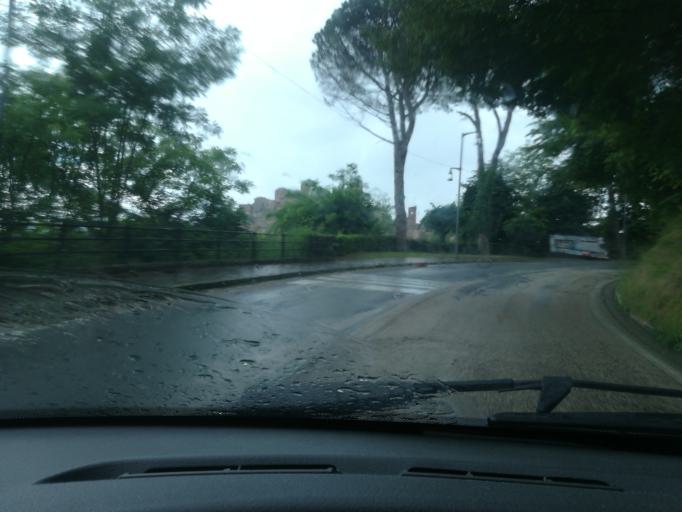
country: IT
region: The Marches
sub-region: Provincia di Macerata
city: Sarnano
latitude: 43.0374
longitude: 13.2976
